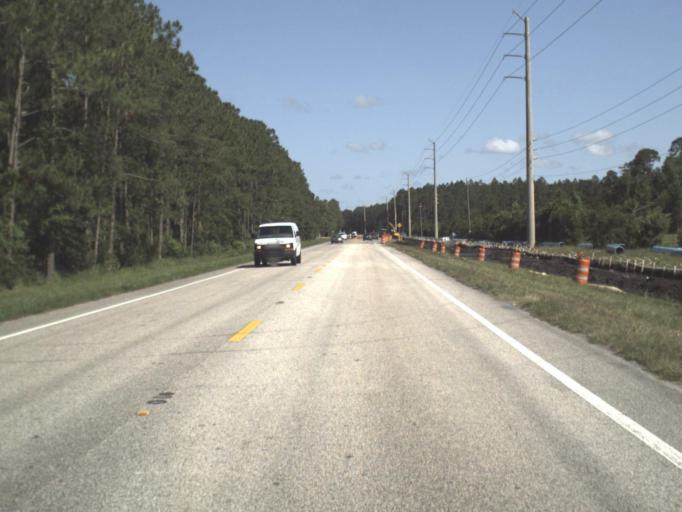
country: US
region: Florida
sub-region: Saint Johns County
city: Saint Augustine
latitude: 29.9406
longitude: -81.4390
